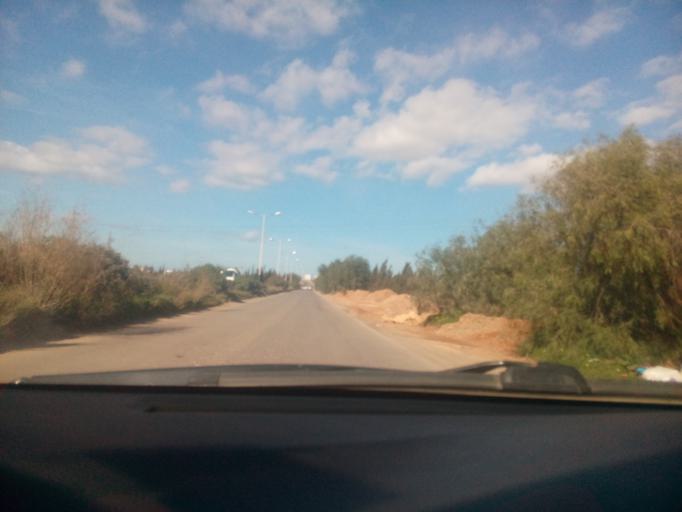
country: DZ
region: Oran
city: Sidi ech Chahmi
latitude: 35.6767
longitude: -0.5659
